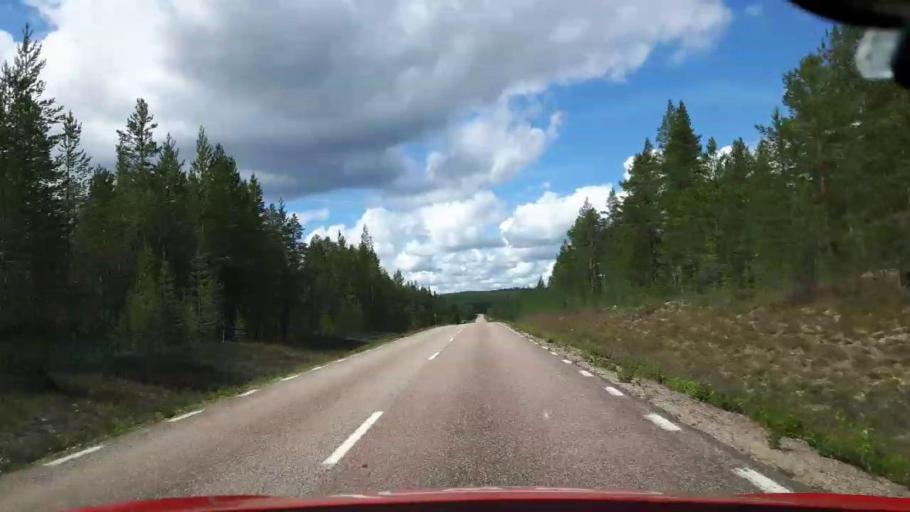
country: SE
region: Jaemtland
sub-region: Harjedalens Kommun
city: Sveg
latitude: 61.8332
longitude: 13.9195
